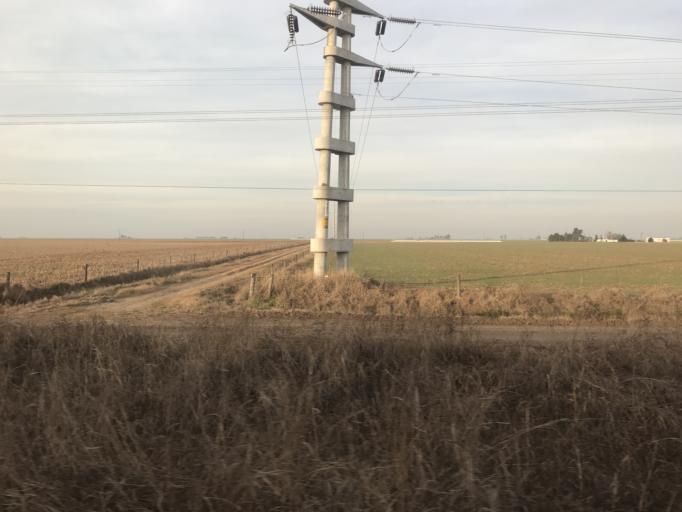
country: AR
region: Cordoba
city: Marcos Juarez
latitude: -32.6847
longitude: -62.1876
